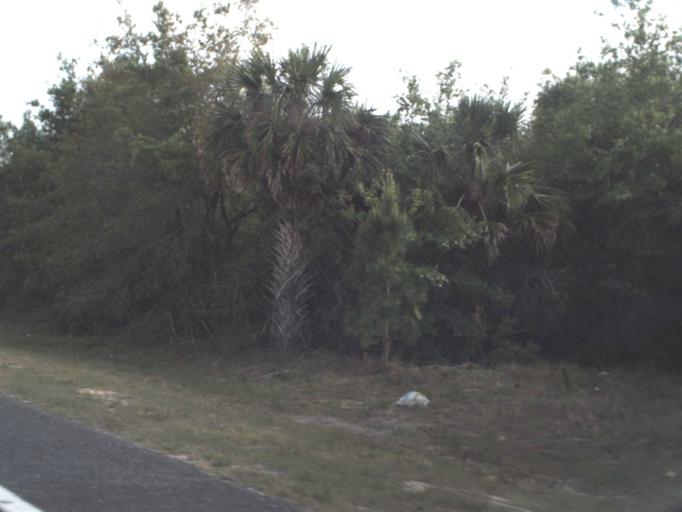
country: US
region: Florida
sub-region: Brevard County
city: Mims
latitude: 28.7139
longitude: -80.8633
